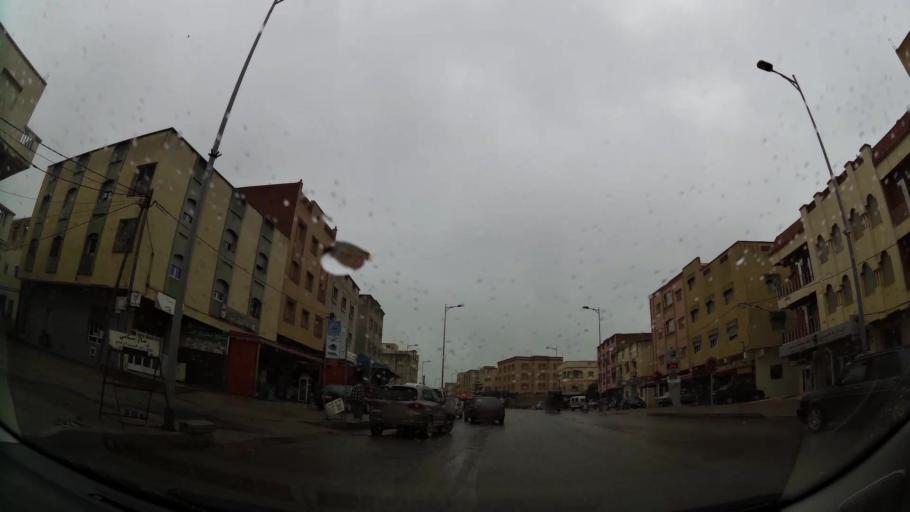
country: MA
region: Oriental
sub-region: Nador
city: Boudinar
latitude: 35.1164
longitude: -3.6413
